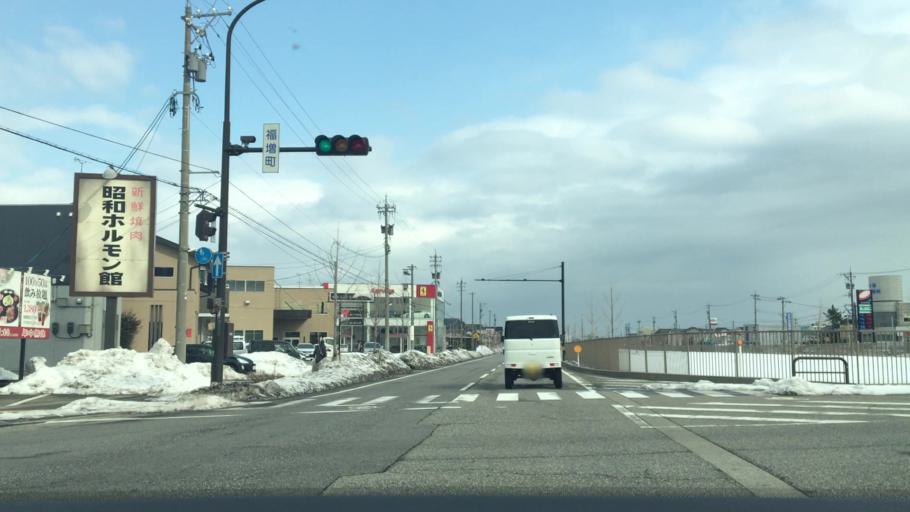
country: JP
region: Ishikawa
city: Nonoichi
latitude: 36.5645
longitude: 136.5804
